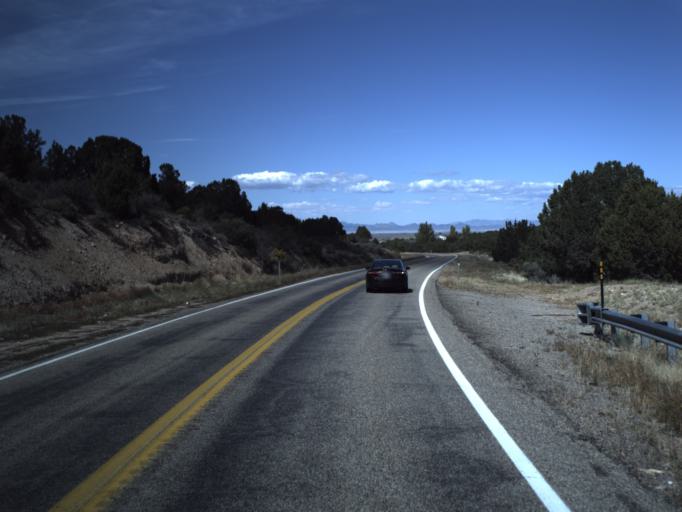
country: US
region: Utah
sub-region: Washington County
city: Enterprise
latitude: 37.5593
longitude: -113.6910
